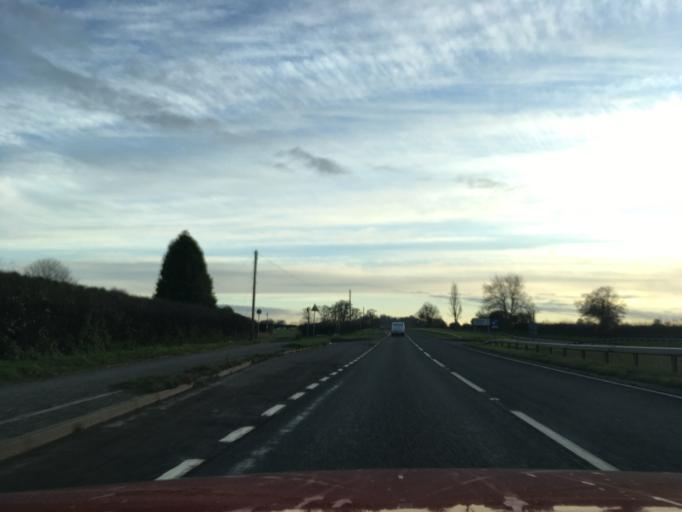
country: GB
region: England
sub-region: Staffordshire
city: Stone
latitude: 52.8724
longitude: -2.1302
